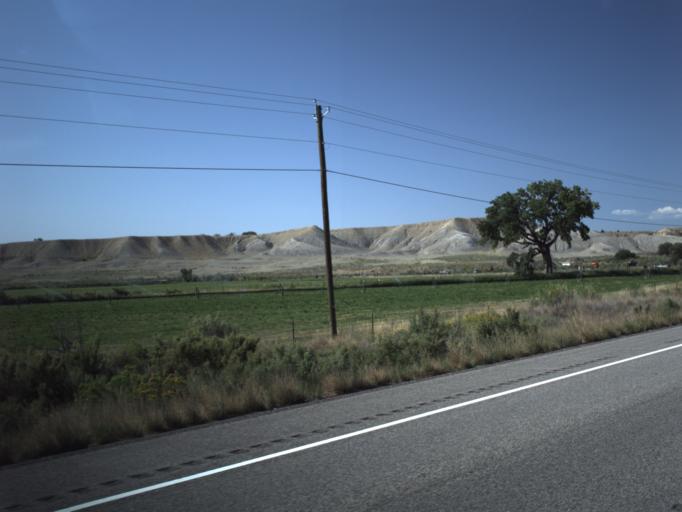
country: US
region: Utah
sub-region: Emery County
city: Orangeville
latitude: 39.1631
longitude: -111.0677
